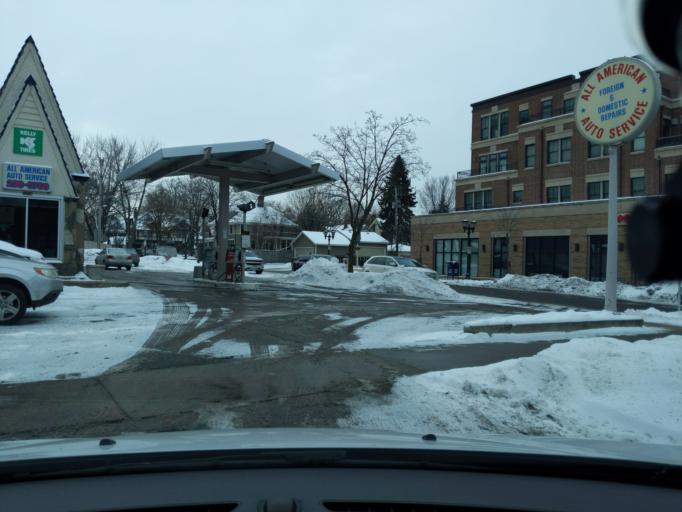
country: US
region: Minnesota
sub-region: Dakota County
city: West Saint Paul
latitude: 44.9400
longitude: -93.1438
